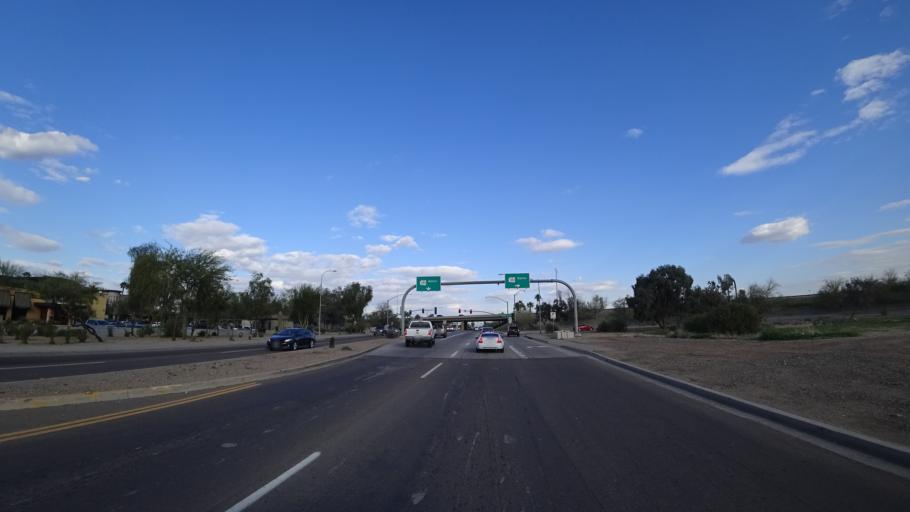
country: US
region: Arizona
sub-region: Maricopa County
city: Peoria
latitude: 33.5514
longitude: -112.2690
